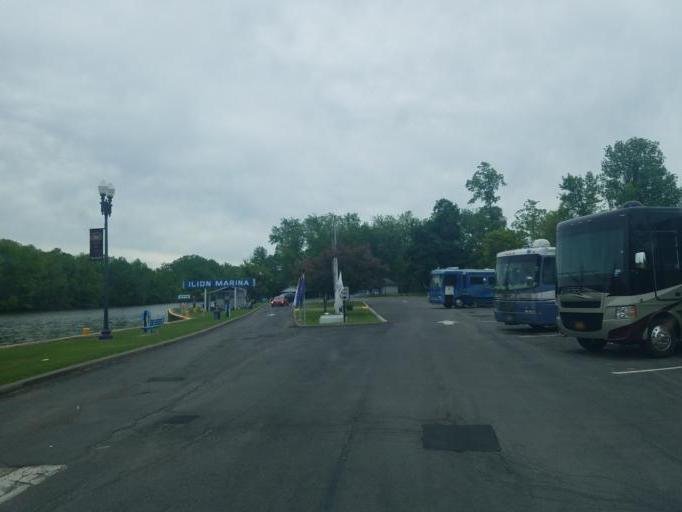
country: US
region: New York
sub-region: Herkimer County
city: Ilion
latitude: 43.0200
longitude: -75.0296
